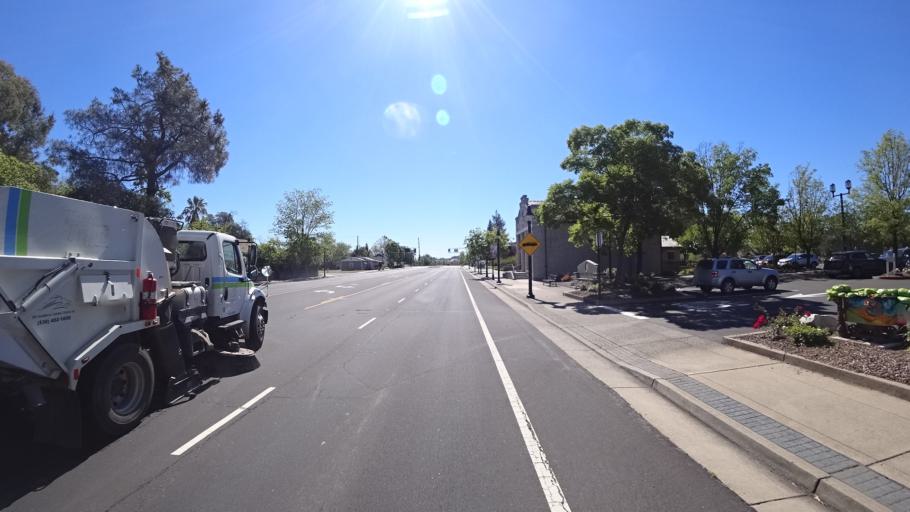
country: US
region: California
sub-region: Placer County
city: Rocklin
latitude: 38.7899
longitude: -121.2344
